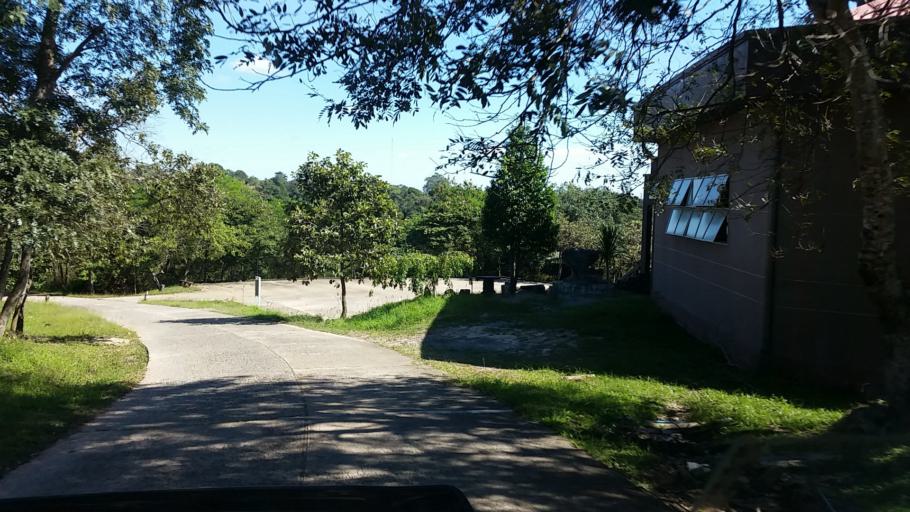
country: TH
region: Chaiyaphum
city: Sap Yai
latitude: 15.6327
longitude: 101.3892
